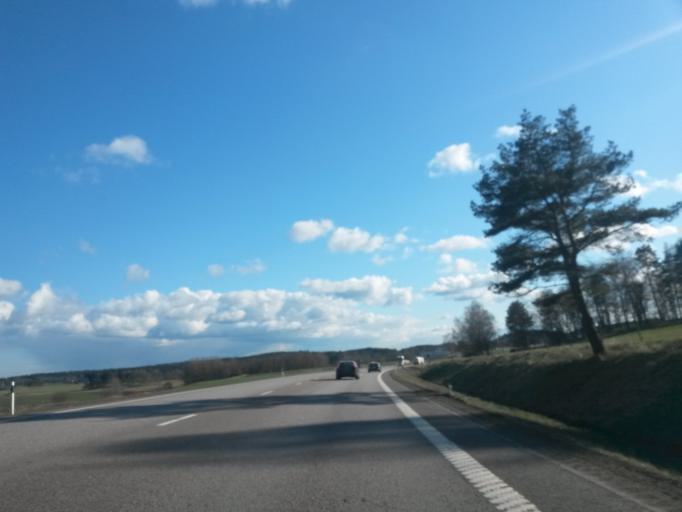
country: SE
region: Vaestra Goetaland
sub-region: Vargarda Kommun
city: Vargarda
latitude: 58.0600
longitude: 12.8193
